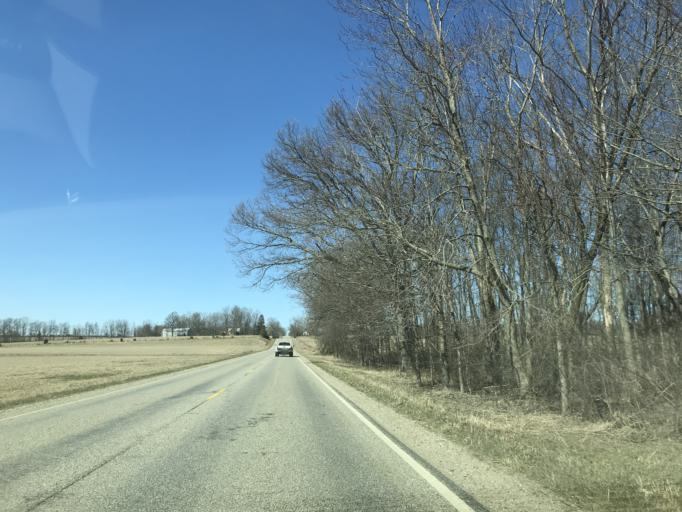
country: US
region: Michigan
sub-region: Hillsdale County
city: Litchfield
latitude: 41.9857
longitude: -84.7733
